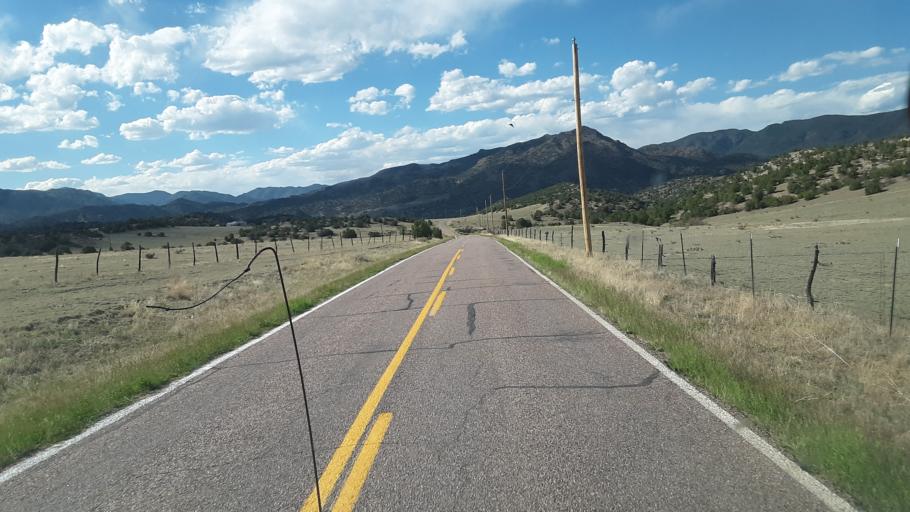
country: US
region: Colorado
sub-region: Fremont County
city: Canon City
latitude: 38.4646
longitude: -105.3768
